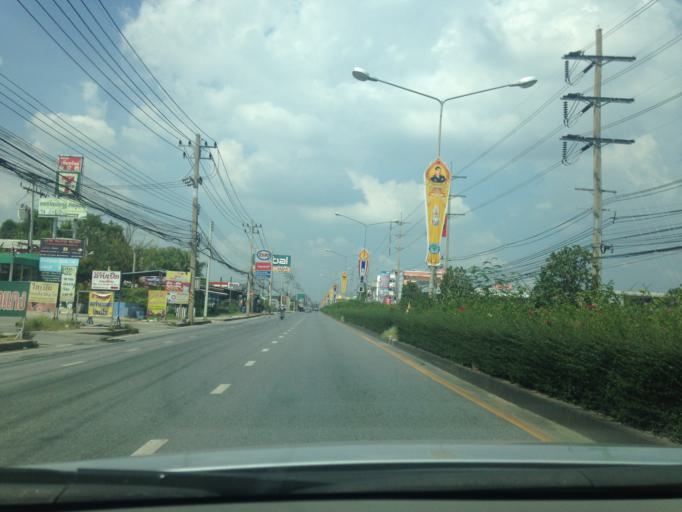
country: TH
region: Pathum Thani
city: Pathum Thani
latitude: 14.0332
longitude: 100.5252
